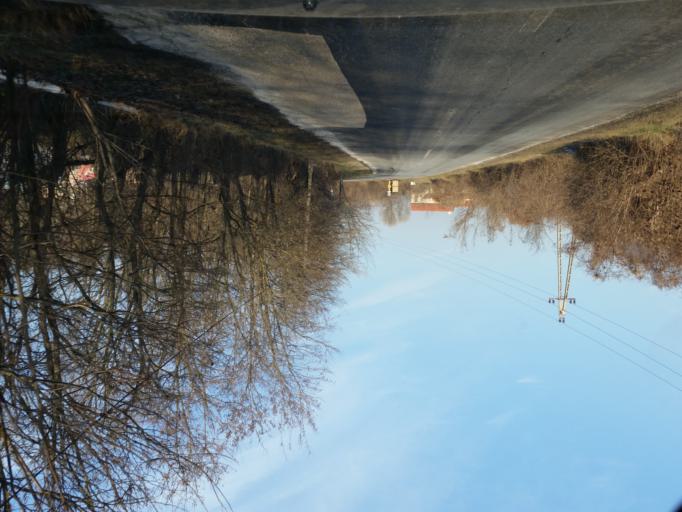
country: HU
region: Pest
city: Paty
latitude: 47.5245
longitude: 18.8359
